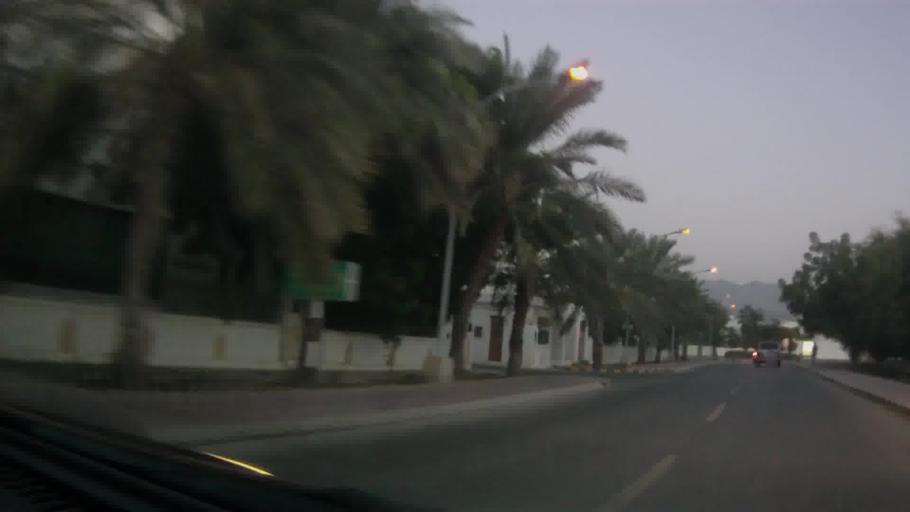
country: OM
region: Muhafazat Masqat
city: Bawshar
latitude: 23.6070
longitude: 58.4434
